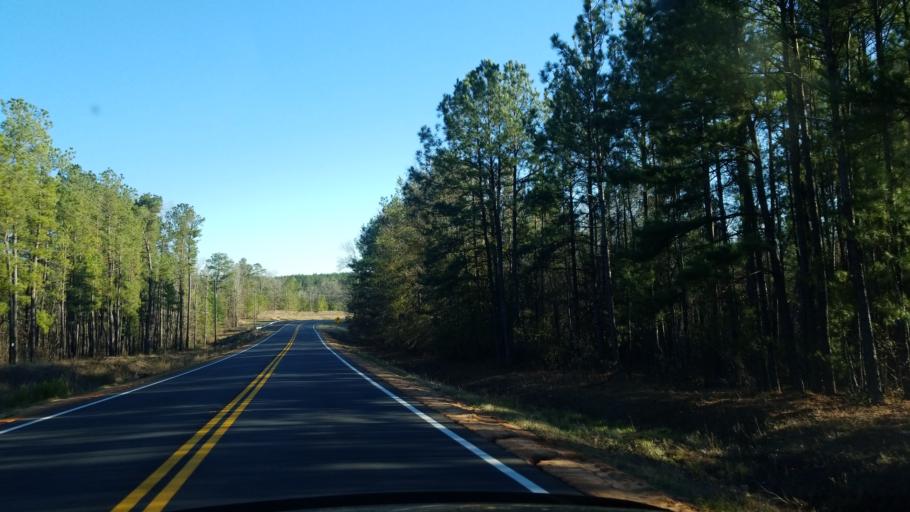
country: US
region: Georgia
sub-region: Talbot County
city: Talbotton
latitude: 32.5549
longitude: -84.5359
